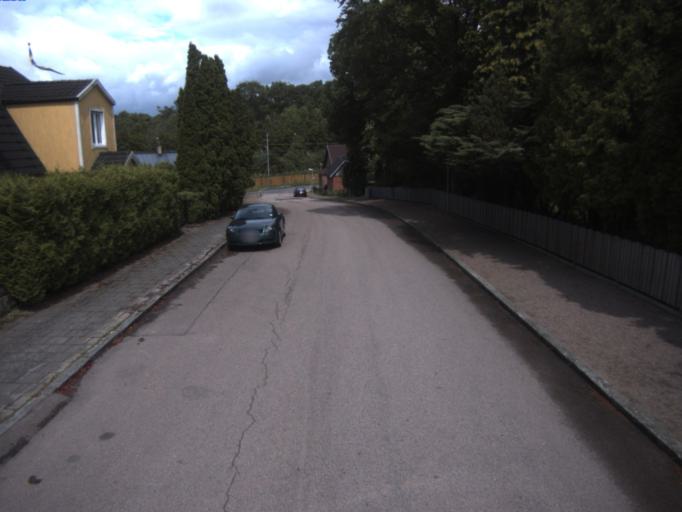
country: SE
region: Skane
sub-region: Helsingborg
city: Rydeback
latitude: 56.0187
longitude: 12.7449
